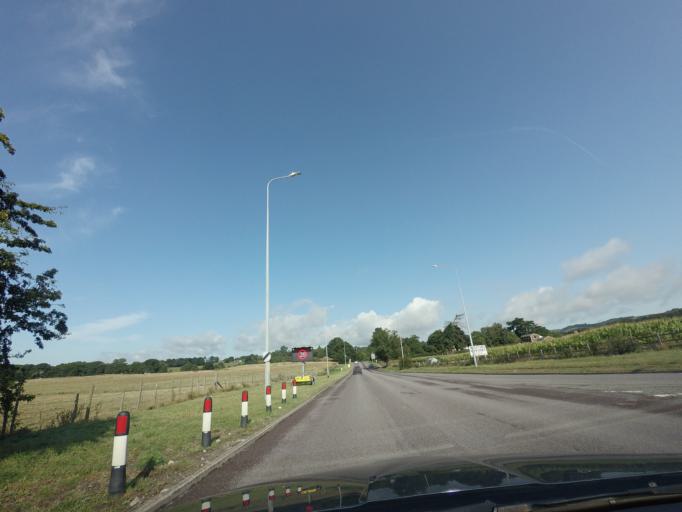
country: GB
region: England
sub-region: Kent
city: Harrietsham
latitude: 51.2620
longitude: 0.6096
